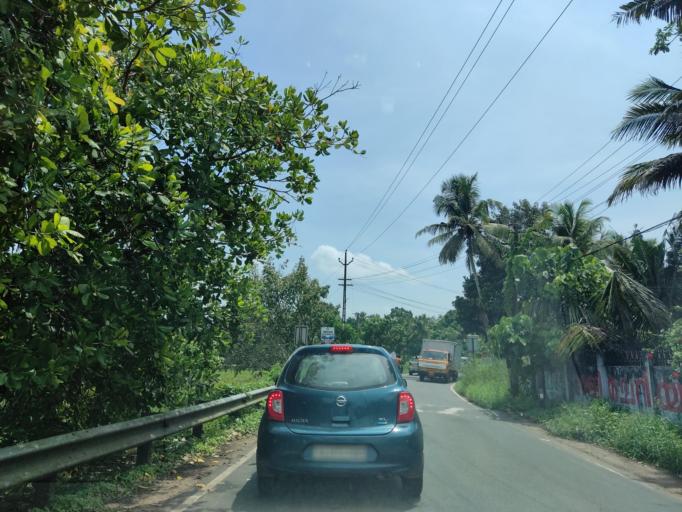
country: IN
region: Kerala
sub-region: Alappuzha
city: Chengannur
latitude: 9.3077
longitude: 76.5949
